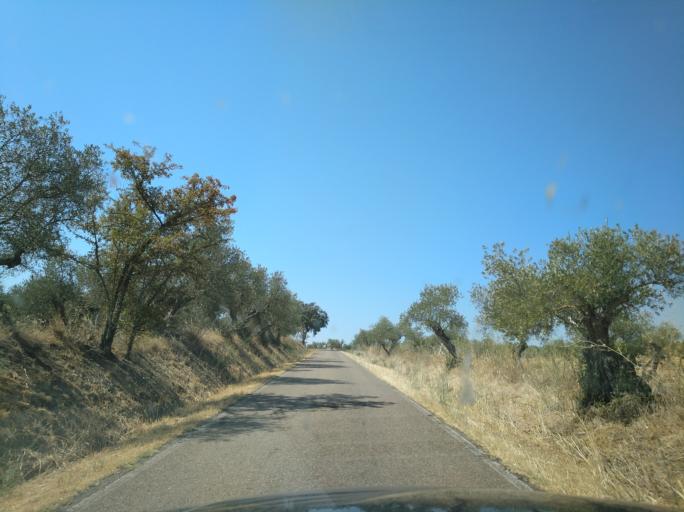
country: PT
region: Portalegre
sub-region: Campo Maior
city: Campo Maior
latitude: 39.0422
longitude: -7.0283
